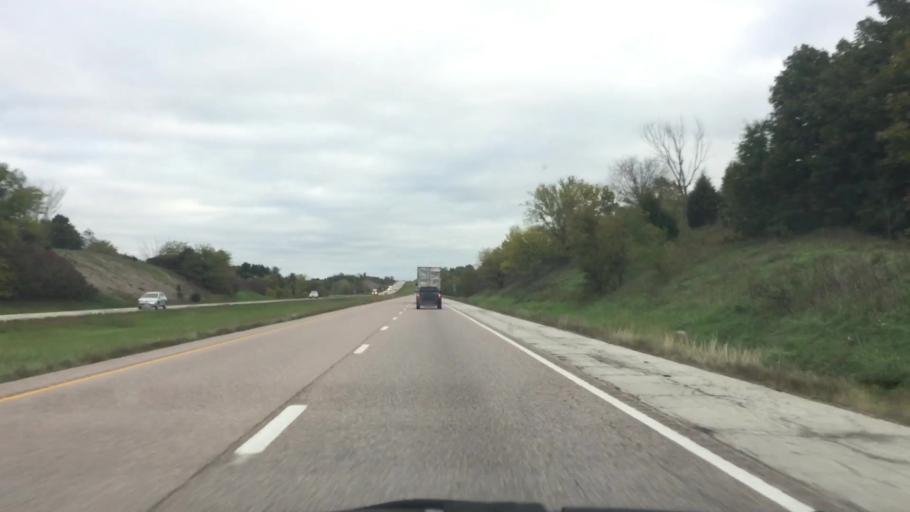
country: US
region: Missouri
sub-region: Clinton County
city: Lathrop
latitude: 39.5017
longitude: -94.2942
